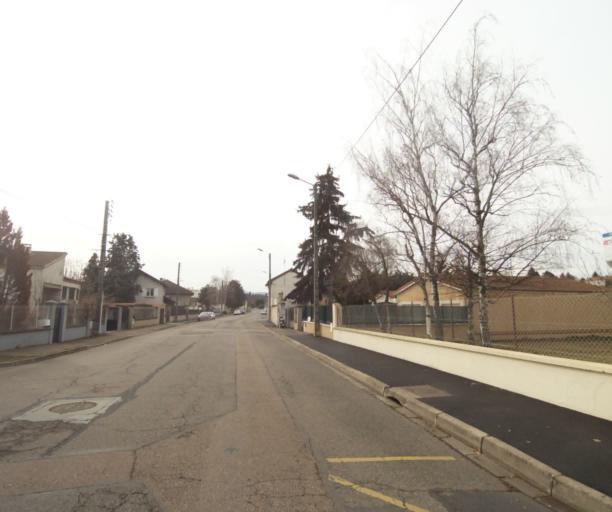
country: FR
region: Rhone-Alpes
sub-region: Departement de la Loire
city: Roanne
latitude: 46.0222
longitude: 4.0582
